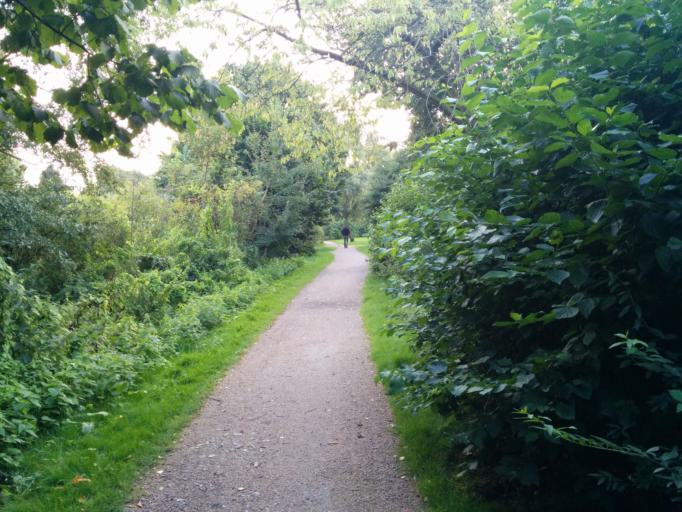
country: DE
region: Hamburg
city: Farmsen-Berne
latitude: 53.6017
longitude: 10.1245
